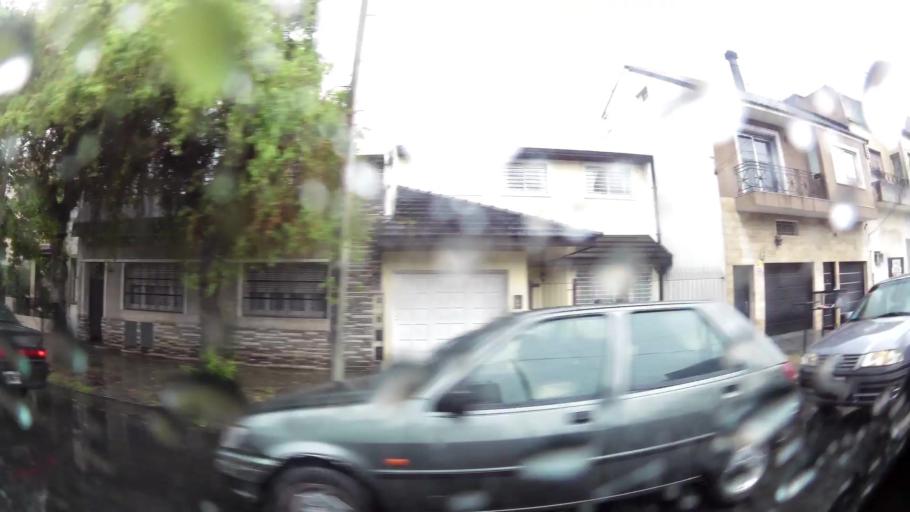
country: AR
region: Buenos Aires
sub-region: Partido de Lanus
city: Lanus
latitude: -34.7258
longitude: -58.4004
